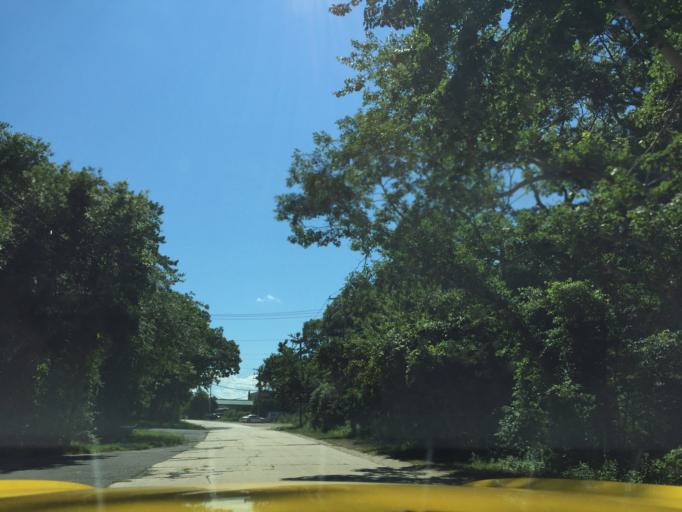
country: US
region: New York
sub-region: Suffolk County
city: East Hampton North
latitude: 40.9509
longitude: -72.2400
